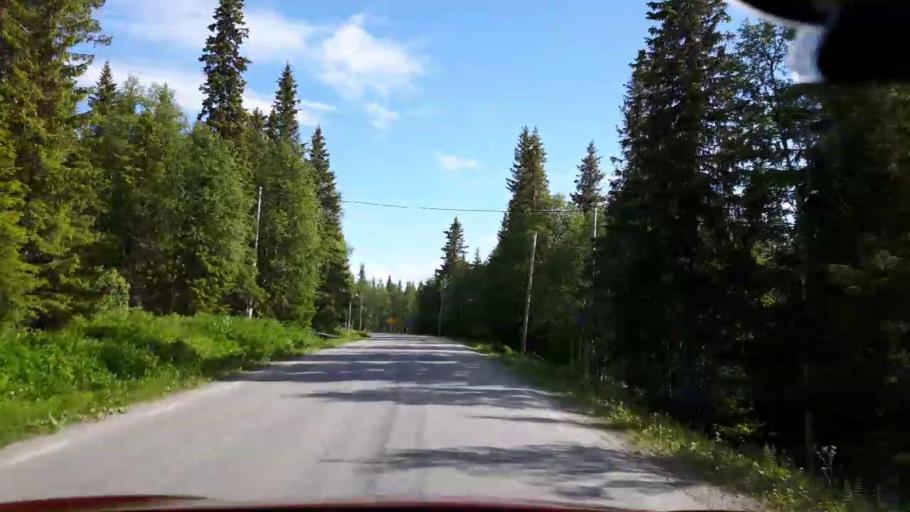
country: SE
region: Jaemtland
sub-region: Krokoms Kommun
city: Valla
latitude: 63.7732
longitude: 14.0469
